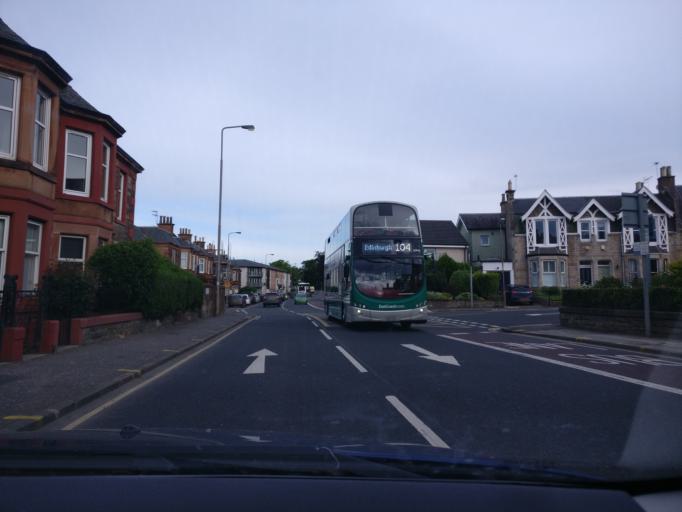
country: GB
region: Scotland
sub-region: West Lothian
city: Seafield
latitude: 55.9535
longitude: -3.1467
